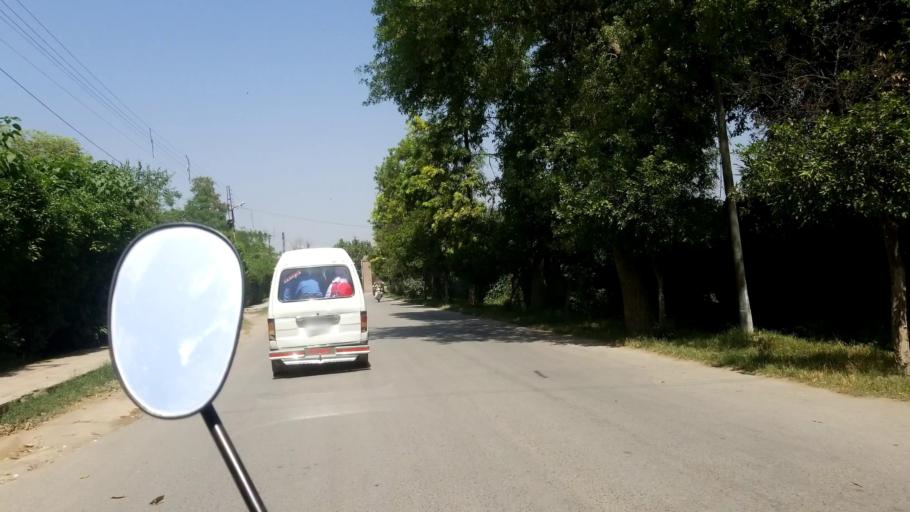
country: PK
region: Khyber Pakhtunkhwa
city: Peshawar
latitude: 34.0130
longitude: 71.4869
